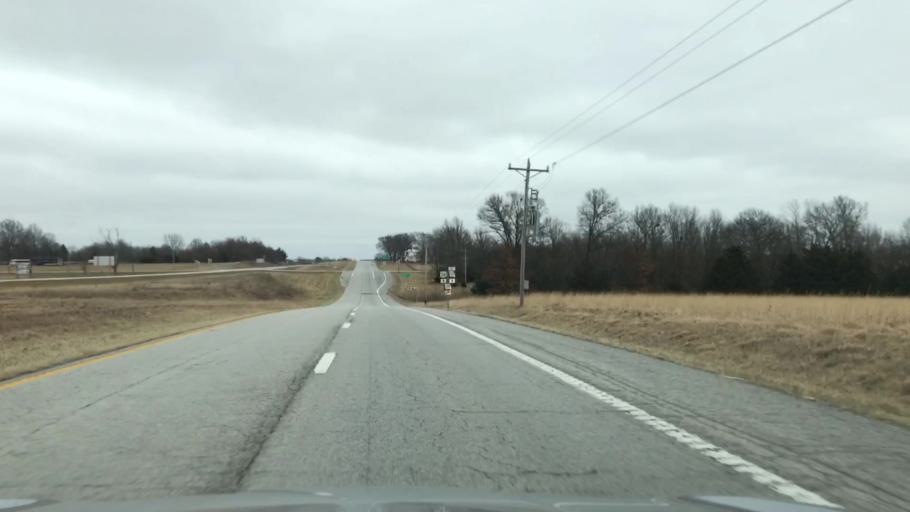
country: US
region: Missouri
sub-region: Linn County
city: Linneus
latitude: 39.7783
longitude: -93.1791
